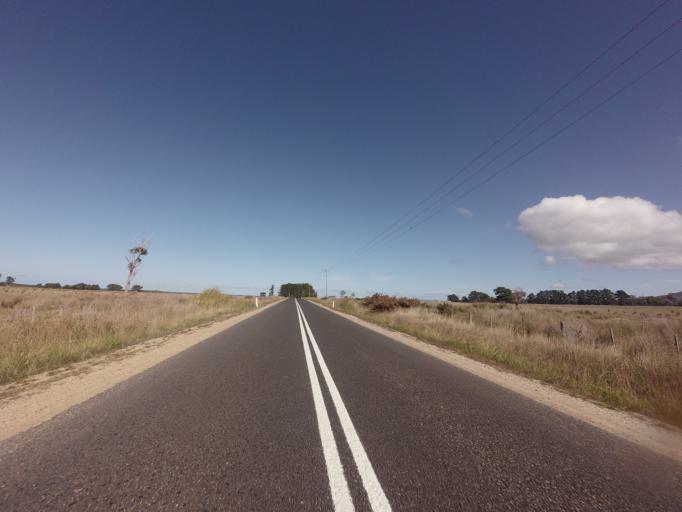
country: AU
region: Tasmania
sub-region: Break O'Day
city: St Helens
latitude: -41.7456
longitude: 148.2748
